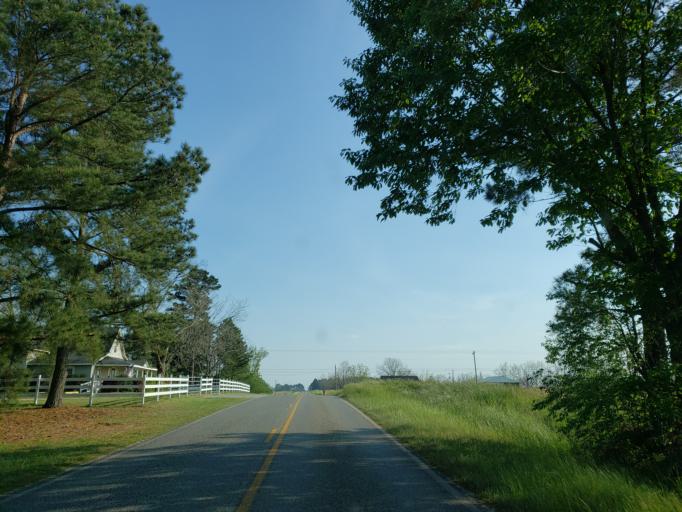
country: US
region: Georgia
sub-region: Tift County
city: Tifton
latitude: 31.5193
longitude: -83.5600
